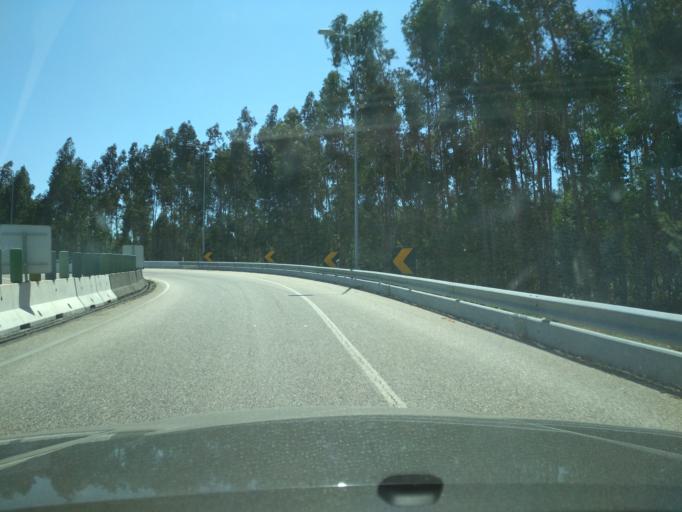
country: PT
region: Leiria
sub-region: Pombal
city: Lourical
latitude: 39.9881
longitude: -8.7887
